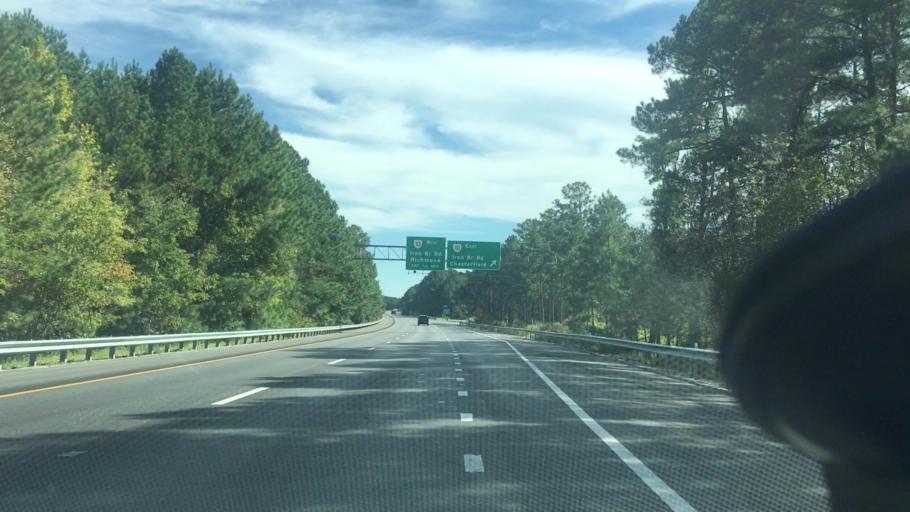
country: US
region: Virginia
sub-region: Chesterfield County
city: Chesterfield
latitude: 37.3952
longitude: -77.5219
